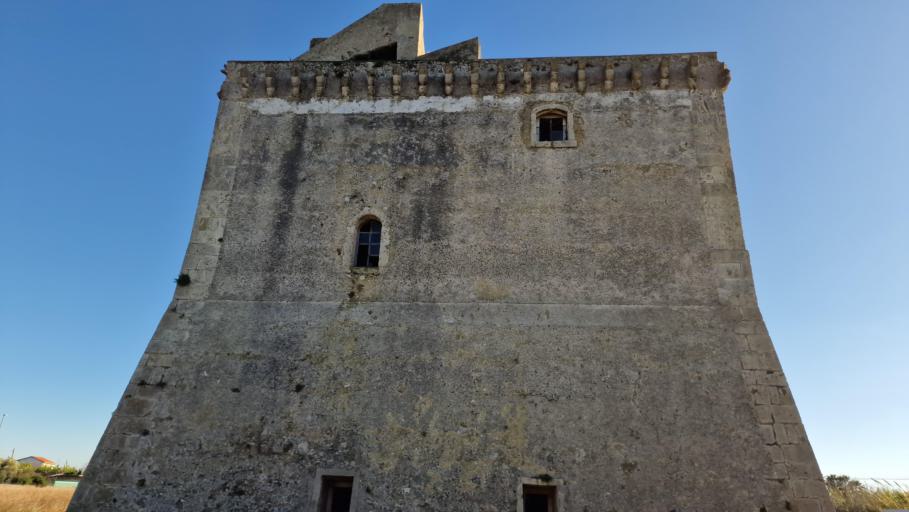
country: IT
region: Calabria
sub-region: Provincia di Catanzaro
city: Santa Eufemia Lamezia
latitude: 38.9306
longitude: 16.2214
